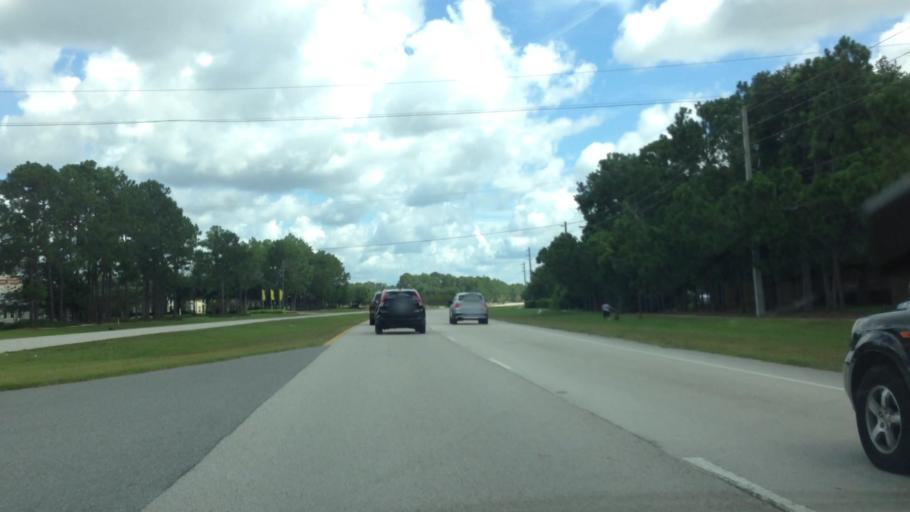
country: US
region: Florida
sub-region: Duval County
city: Jacksonville Beach
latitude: 30.2607
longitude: -81.4665
